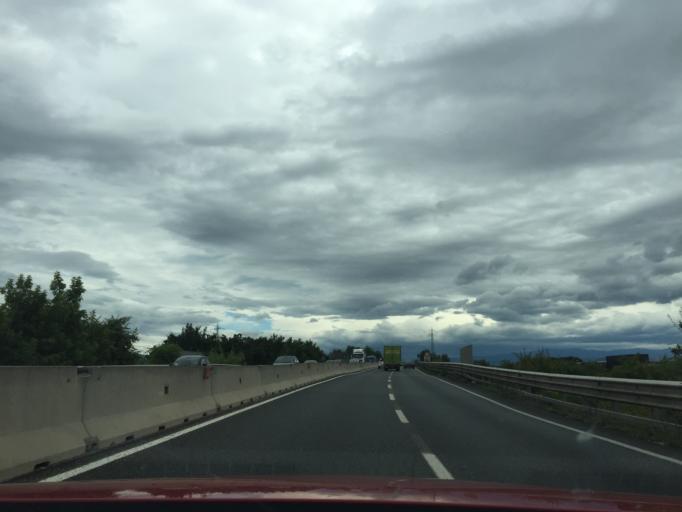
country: IT
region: Tuscany
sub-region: Province of Florence
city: Lastra a Signa
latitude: 43.7731
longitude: 11.1313
